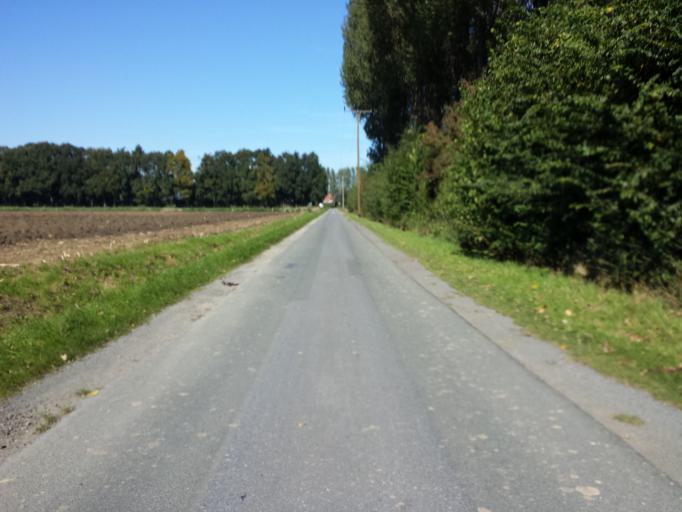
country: DE
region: North Rhine-Westphalia
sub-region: Regierungsbezirk Detmold
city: Langenberg
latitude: 51.7835
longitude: 8.3368
